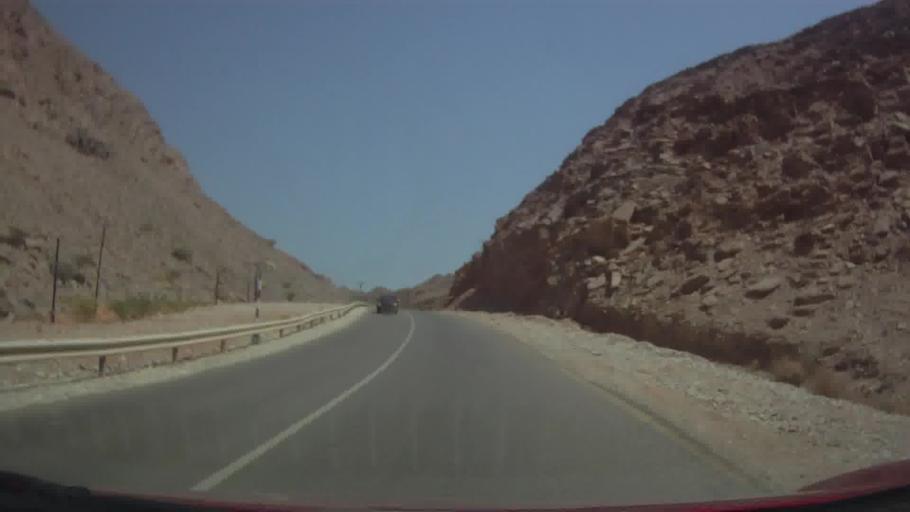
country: OM
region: Muhafazat Masqat
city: Muscat
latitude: 23.5092
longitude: 58.6710
